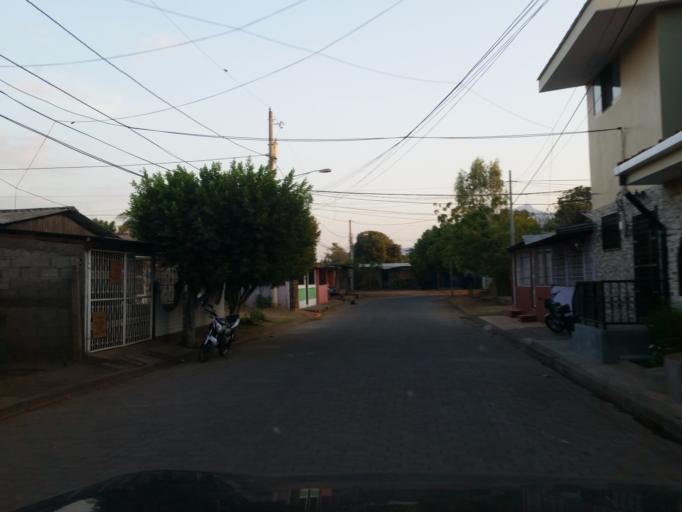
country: NI
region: Granada
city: Granada
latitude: 11.9482
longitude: -85.9465
